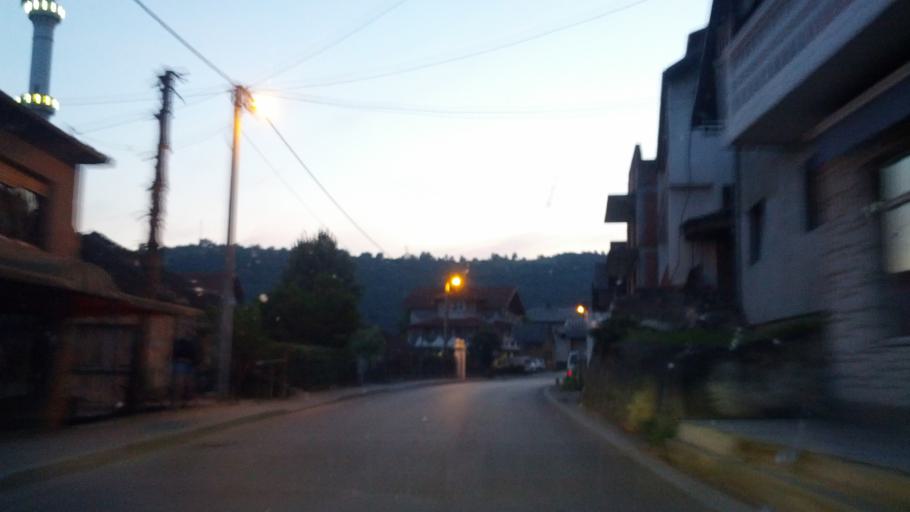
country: BA
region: Federation of Bosnia and Herzegovina
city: Bosanska Krupa
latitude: 44.8871
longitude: 16.1497
